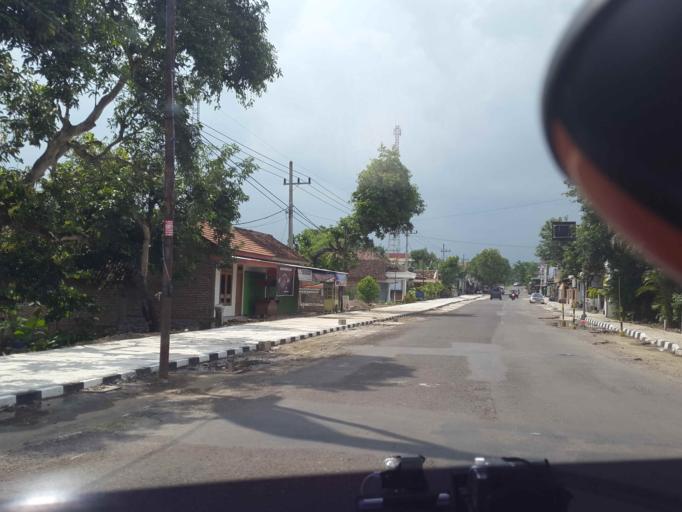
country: ID
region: East Java
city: Ponorogo
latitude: -7.7602
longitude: 111.3999
